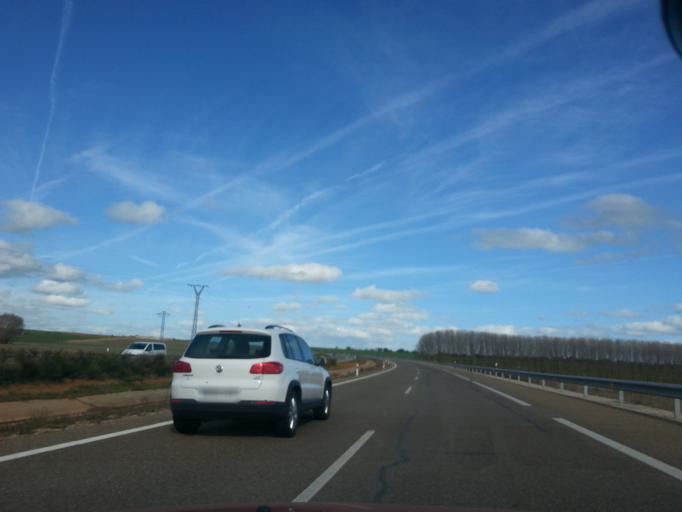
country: ES
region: Castille and Leon
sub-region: Provincia de Salamanca
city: Calzada de Don Diego
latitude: 40.9065
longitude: -5.8787
